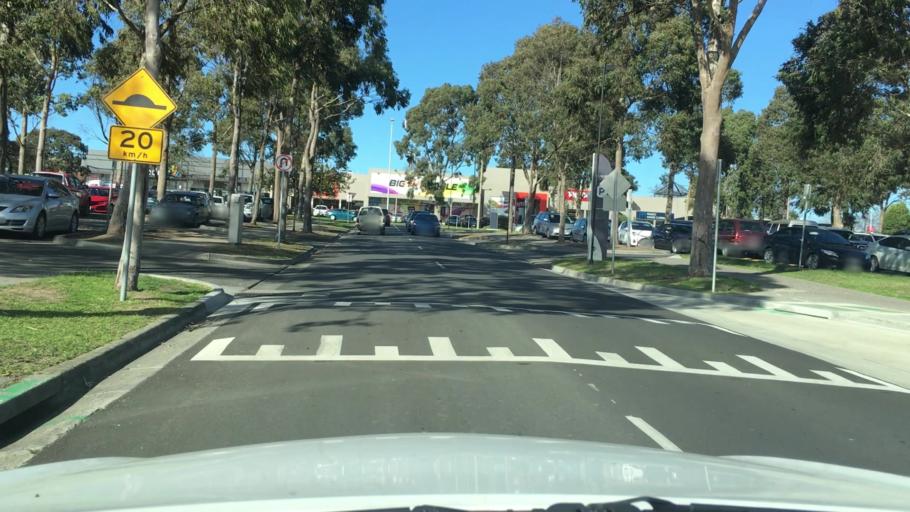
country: AU
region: Victoria
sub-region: Casey
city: Narre Warren
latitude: -38.0200
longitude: 145.3013
